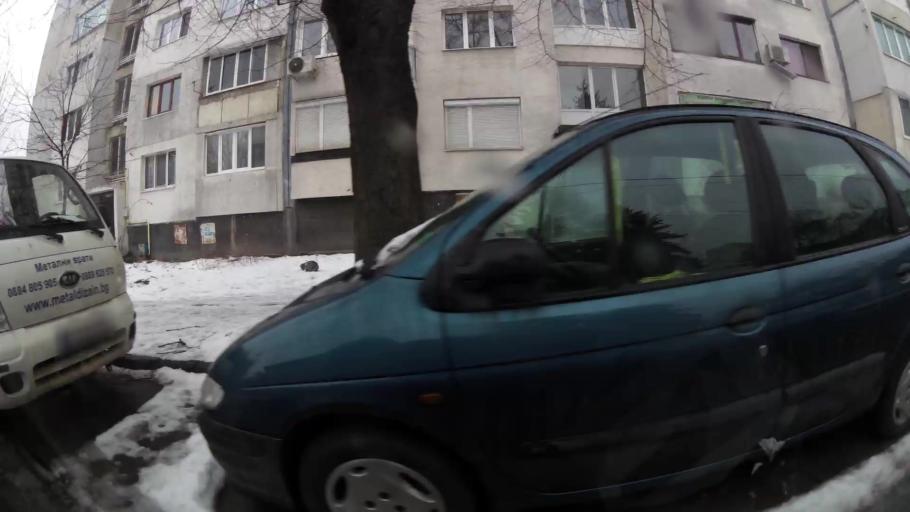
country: BG
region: Sofia-Capital
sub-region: Stolichna Obshtina
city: Sofia
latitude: 42.6655
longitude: 23.2715
